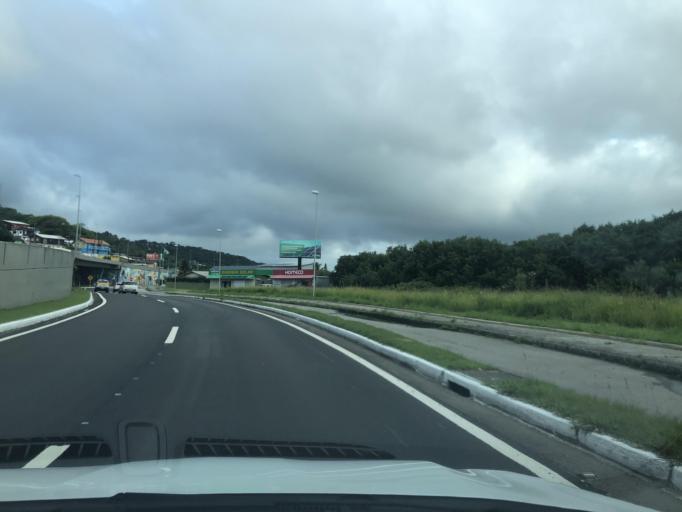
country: BR
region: Santa Catarina
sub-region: Florianopolis
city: Costeira do Pirajubae
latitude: -27.6460
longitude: -48.5232
